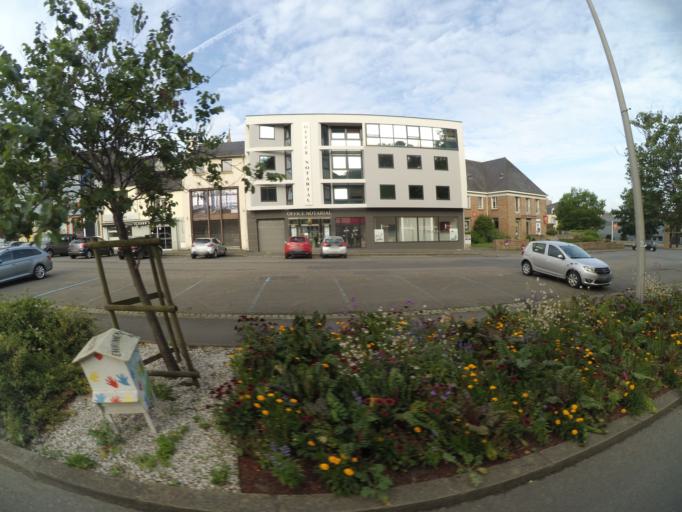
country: FR
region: Brittany
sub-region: Departement des Cotes-d'Armor
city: Guingamp
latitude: 48.5618
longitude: -3.1490
